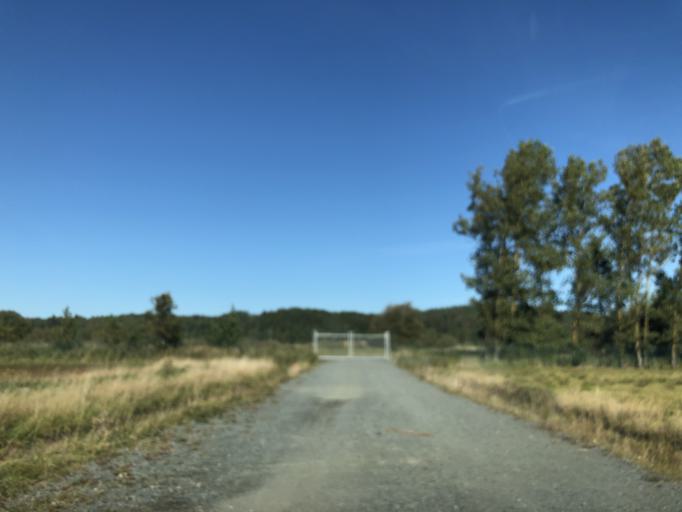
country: SE
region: Vaestra Goetaland
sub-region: Goteborg
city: Goeteborg
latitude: 57.7729
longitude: 11.9201
